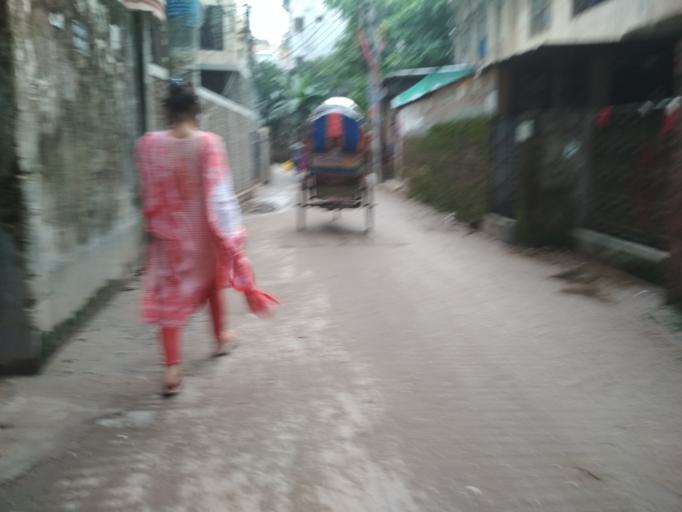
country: BD
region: Dhaka
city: Azimpur
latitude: 23.8045
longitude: 90.3675
